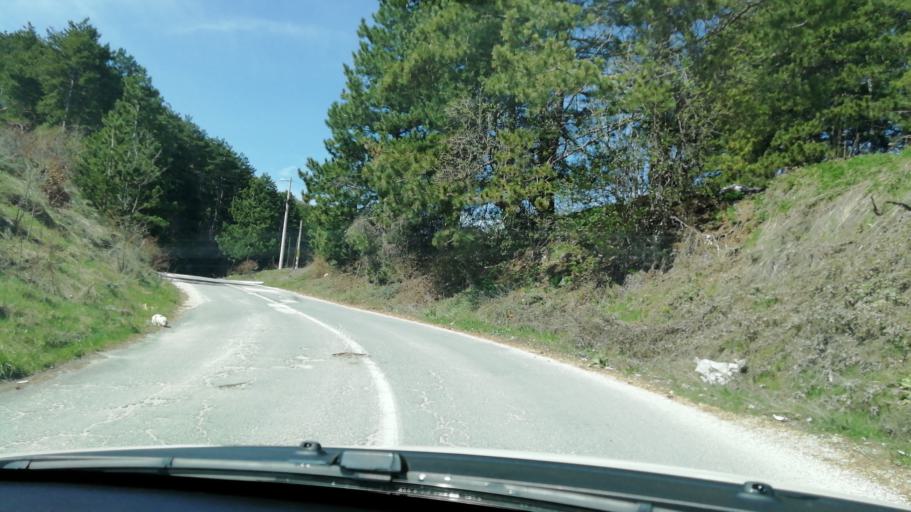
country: MK
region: Krusevo
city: Krushevo
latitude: 41.3651
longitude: 21.2558
